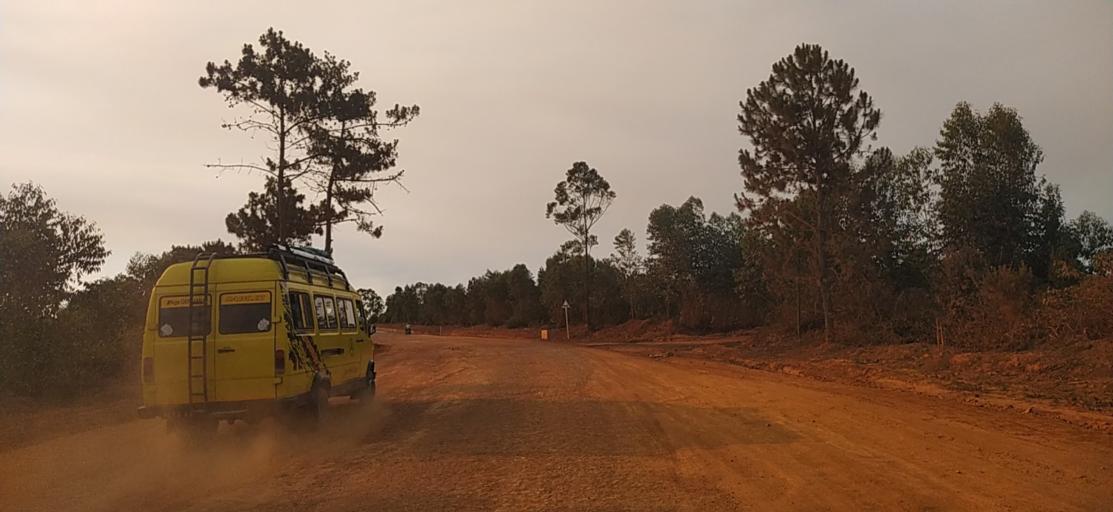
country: MG
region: Alaotra Mangoro
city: Moramanga
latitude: -18.5754
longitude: 48.2699
